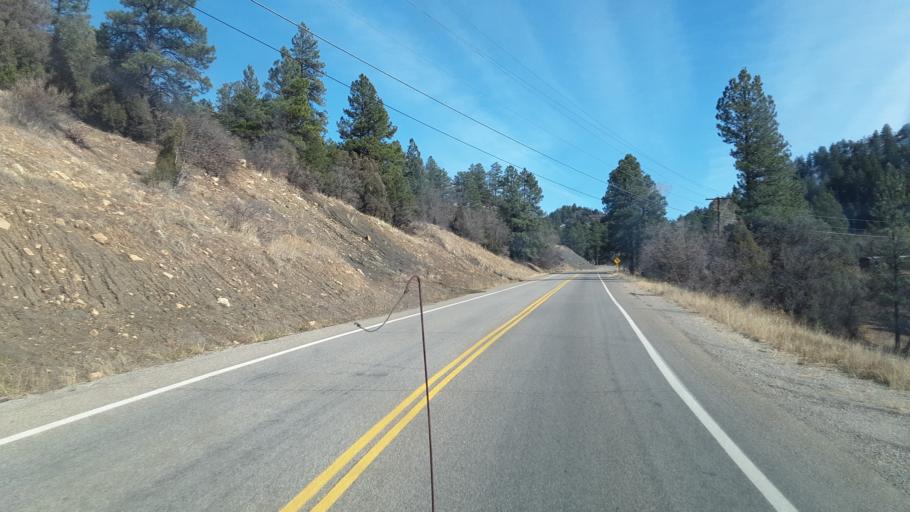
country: US
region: Colorado
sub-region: La Plata County
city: Durango
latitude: 37.3068
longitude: -107.8220
